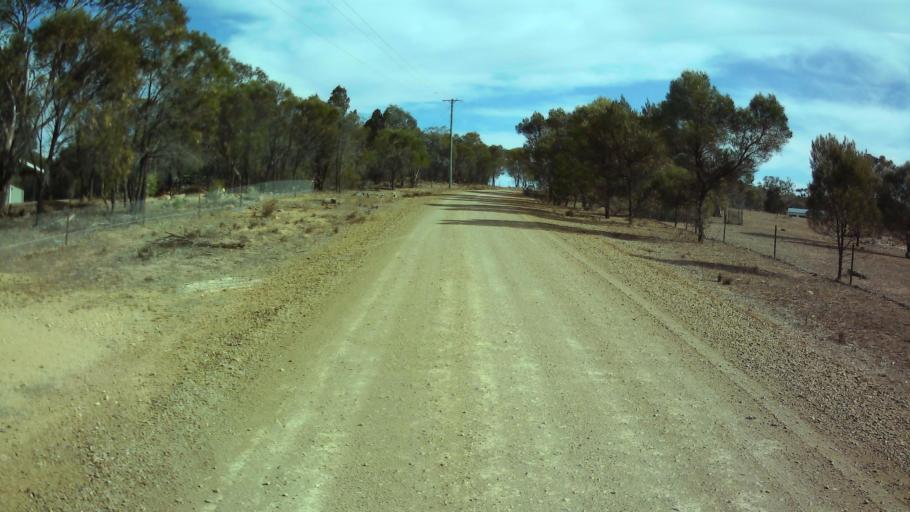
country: AU
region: New South Wales
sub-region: Weddin
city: Grenfell
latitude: -33.8729
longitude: 148.1922
